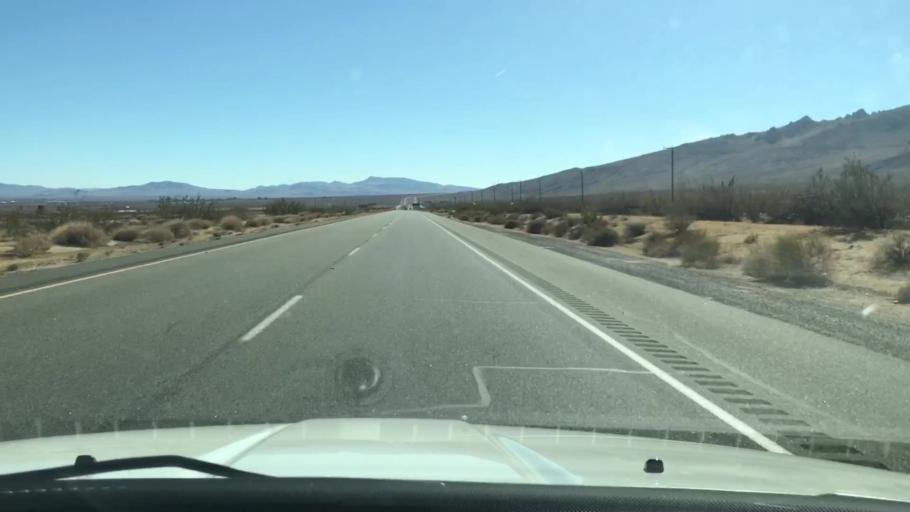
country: US
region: California
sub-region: Kern County
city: Inyokern
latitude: 35.7318
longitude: -117.8695
